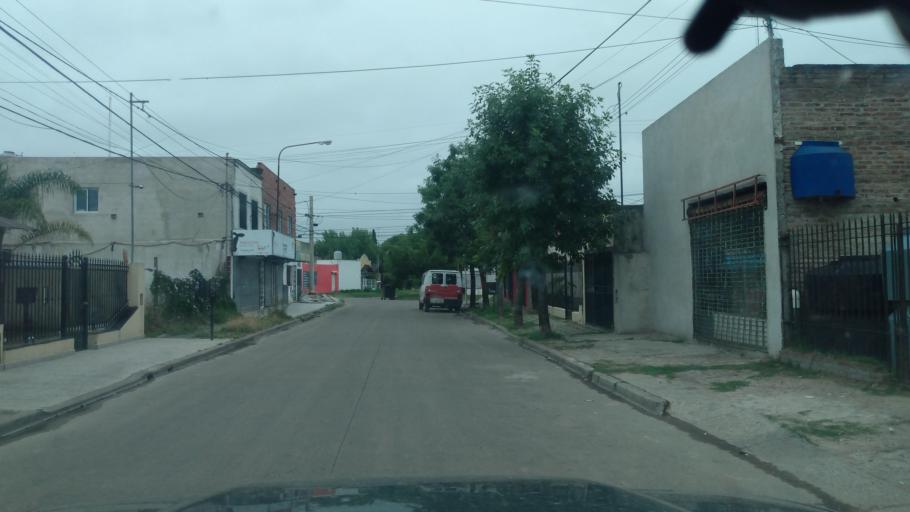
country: AR
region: Buenos Aires
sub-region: Partido de Lujan
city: Lujan
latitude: -34.5772
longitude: -59.1205
